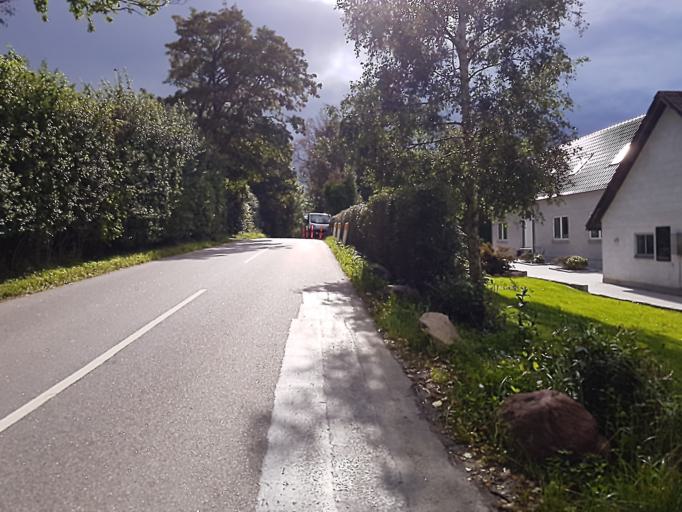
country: DK
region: Zealand
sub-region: Roskilde Kommune
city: Gundsomagle
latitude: 55.7258
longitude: 12.1395
